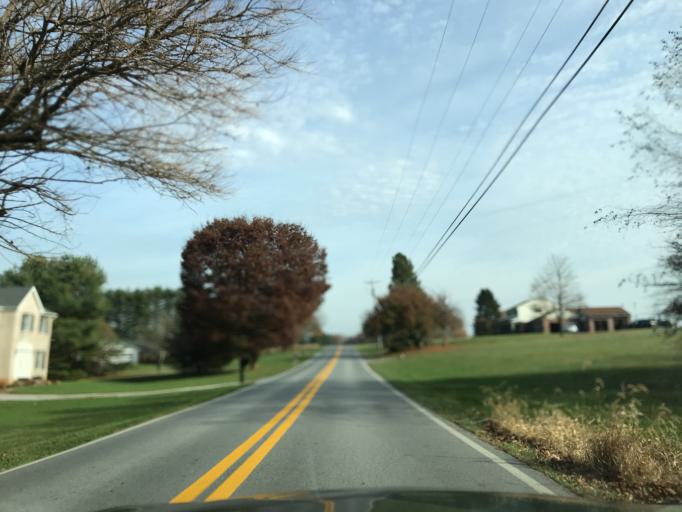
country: US
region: Maryland
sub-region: Carroll County
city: Eldersburg
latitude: 39.4934
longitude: -76.9215
